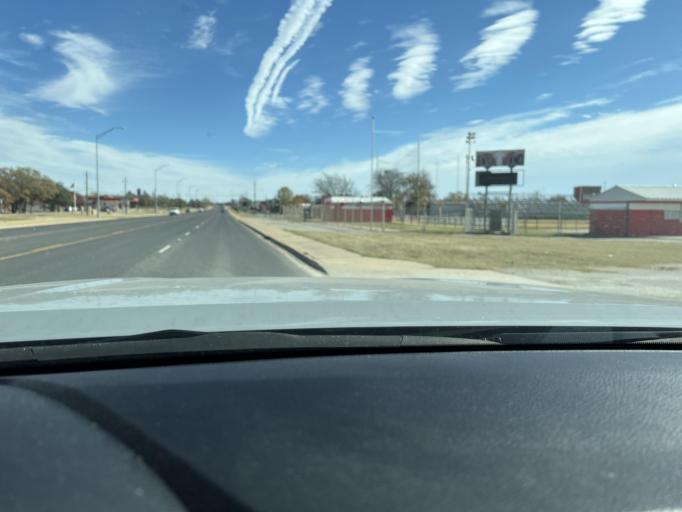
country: US
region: Texas
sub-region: Eastland County
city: Eastland
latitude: 32.4017
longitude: -98.8089
